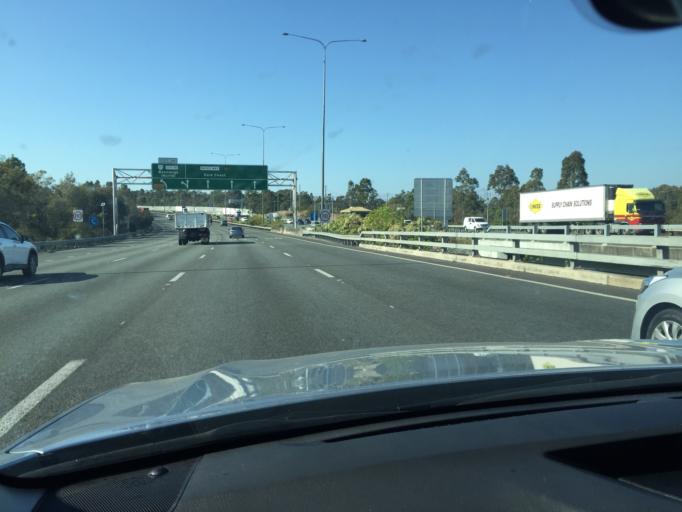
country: AU
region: Queensland
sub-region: Logan
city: Beenleigh
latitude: -27.6978
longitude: 153.1959
